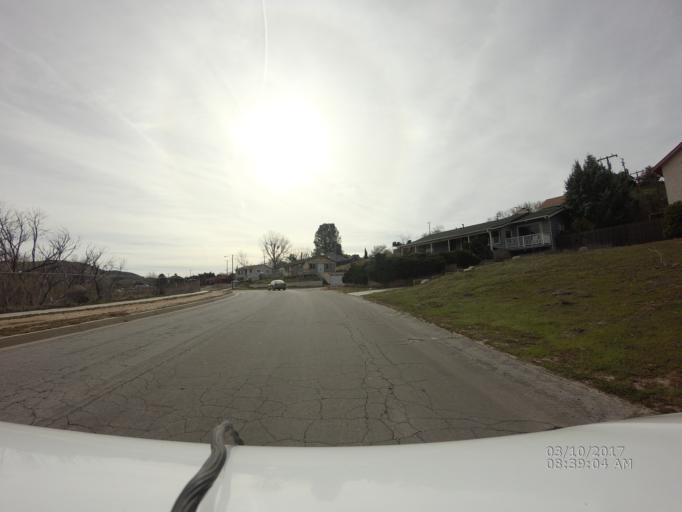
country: US
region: California
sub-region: Los Angeles County
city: Green Valley
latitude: 34.6622
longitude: -118.3952
